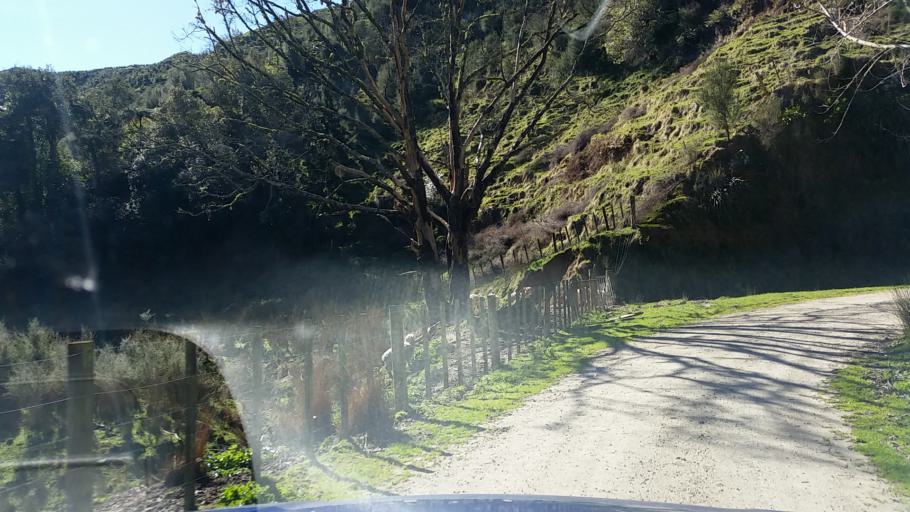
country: NZ
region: Manawatu-Wanganui
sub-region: Wanganui District
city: Wanganui
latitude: -39.6762
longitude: 174.8558
